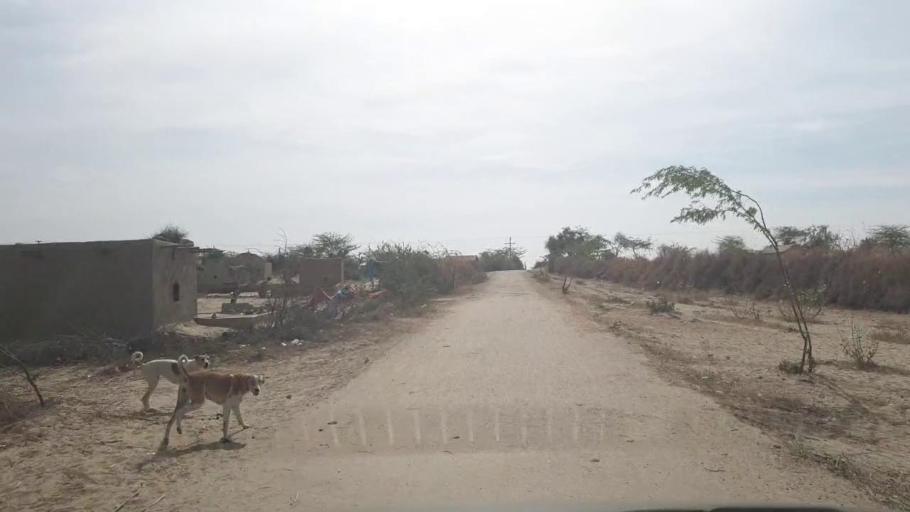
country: PK
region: Sindh
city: Umarkot
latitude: 25.2989
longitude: 69.7418
